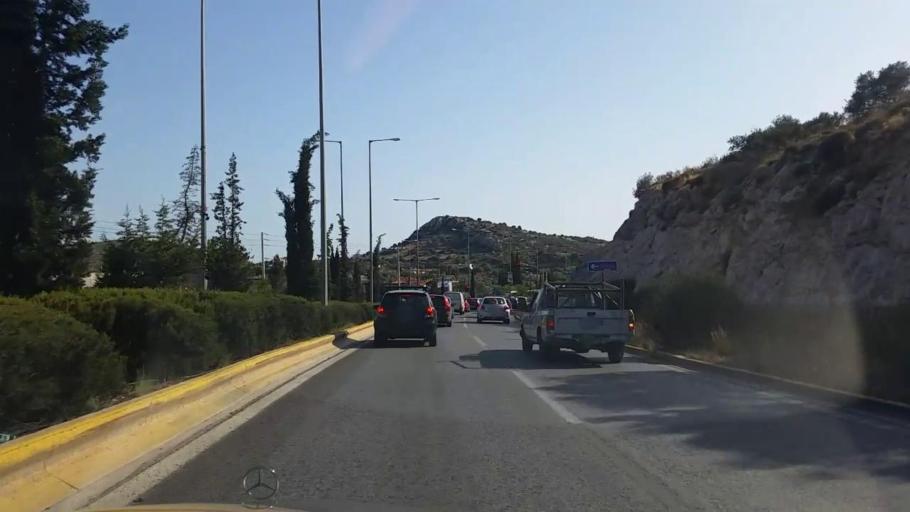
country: GR
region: Attica
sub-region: Nomarchia Anatolikis Attikis
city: Kitsi
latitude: 37.8595
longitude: 23.8423
